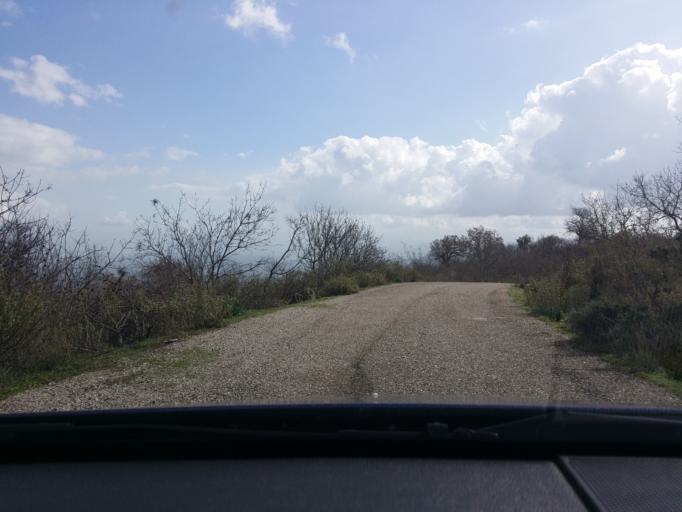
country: GR
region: West Greece
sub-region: Nomos Aitolias kai Akarnanias
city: Fitiai
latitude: 38.6375
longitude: 21.1971
